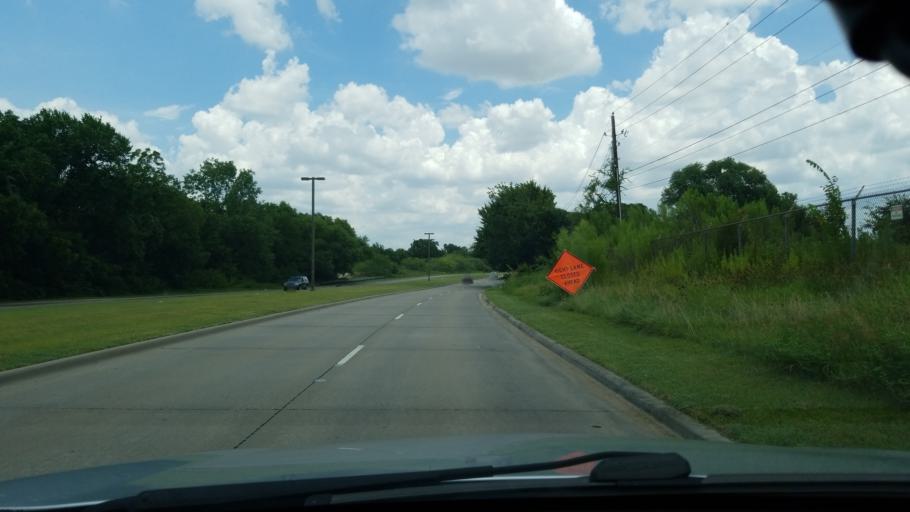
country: US
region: Texas
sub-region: Dallas County
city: Coppell
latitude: 32.9550
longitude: -96.9758
